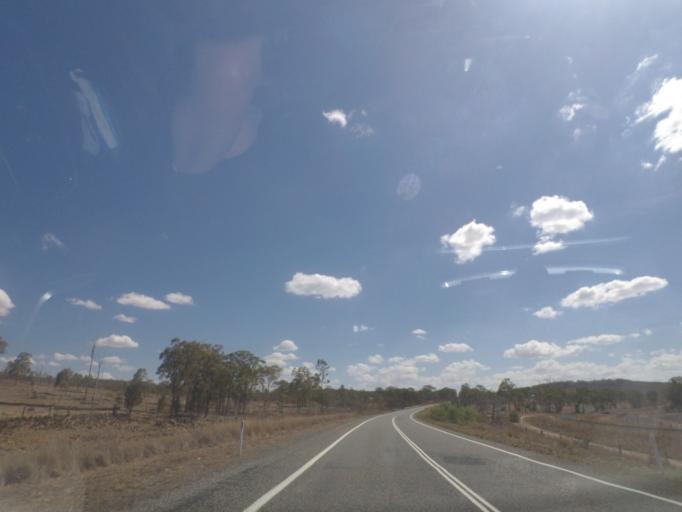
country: AU
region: Queensland
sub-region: Southern Downs
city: Warwick
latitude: -28.2164
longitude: 151.5619
